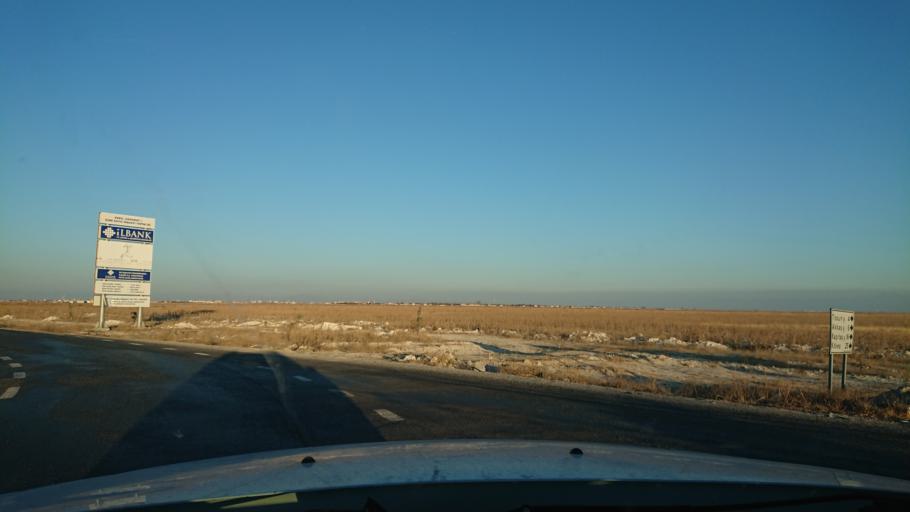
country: TR
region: Aksaray
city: Eskil
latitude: 38.3757
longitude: 33.3720
